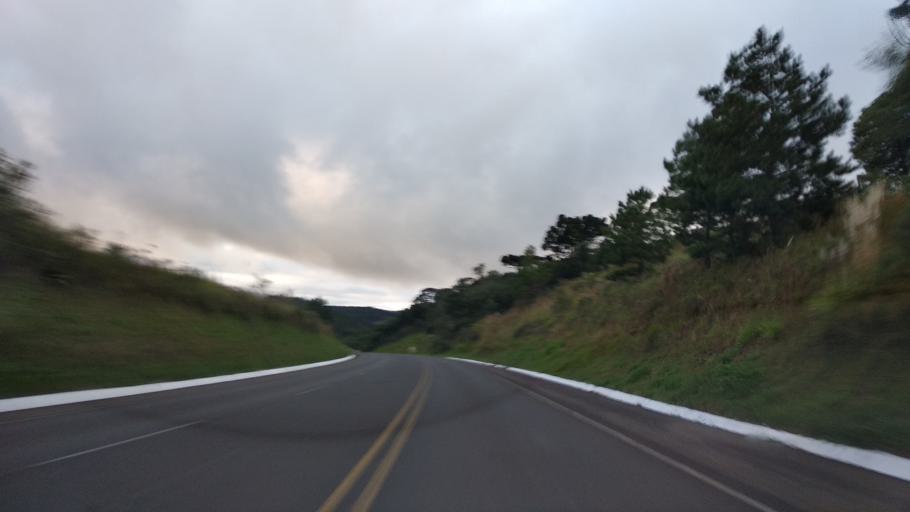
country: BR
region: Santa Catarina
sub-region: Campos Novos
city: Campos Novos
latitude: -27.4461
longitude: -51.0023
